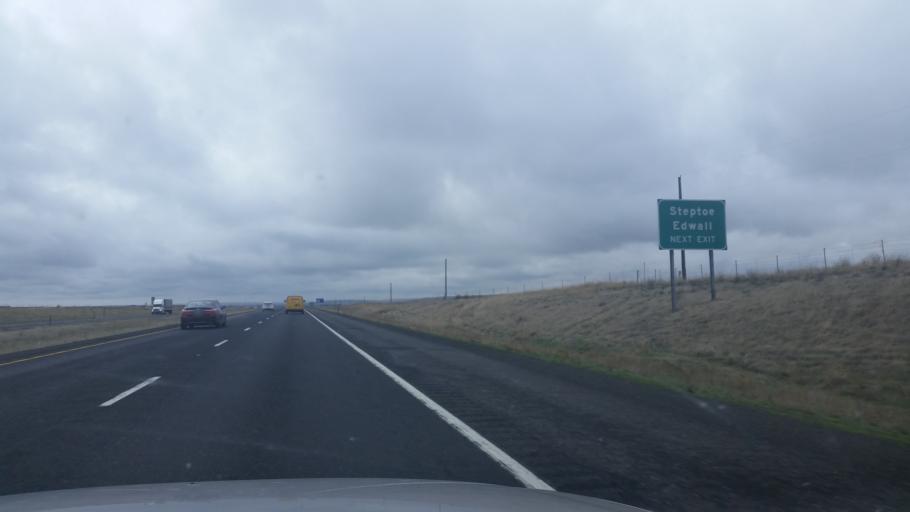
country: US
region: Washington
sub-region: Spokane County
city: Medical Lake
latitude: 47.3152
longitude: -117.9579
